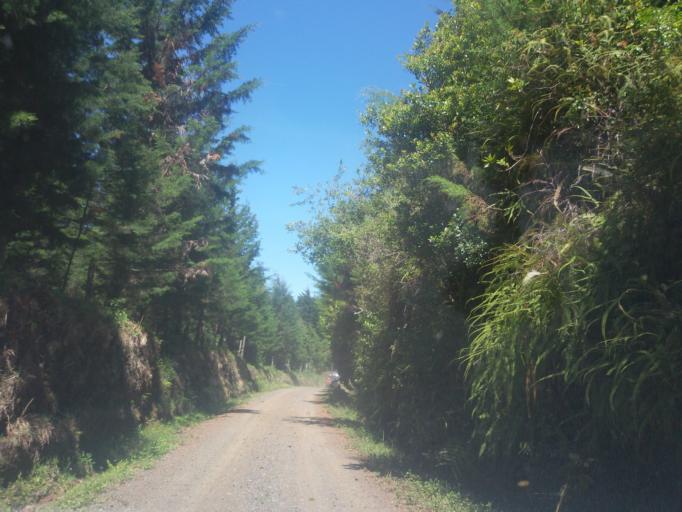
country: CR
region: Heredia
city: San Josecito
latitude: 10.0784
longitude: -84.0943
